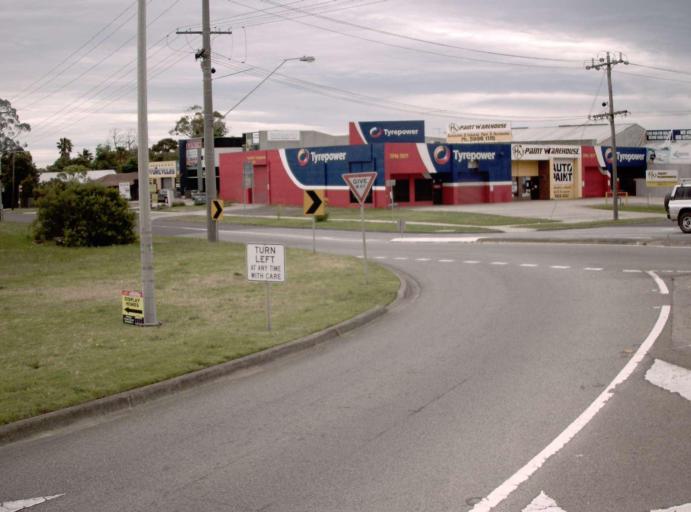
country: AU
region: Victoria
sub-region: Casey
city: Cranbourne
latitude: -38.0978
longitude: 145.2832
